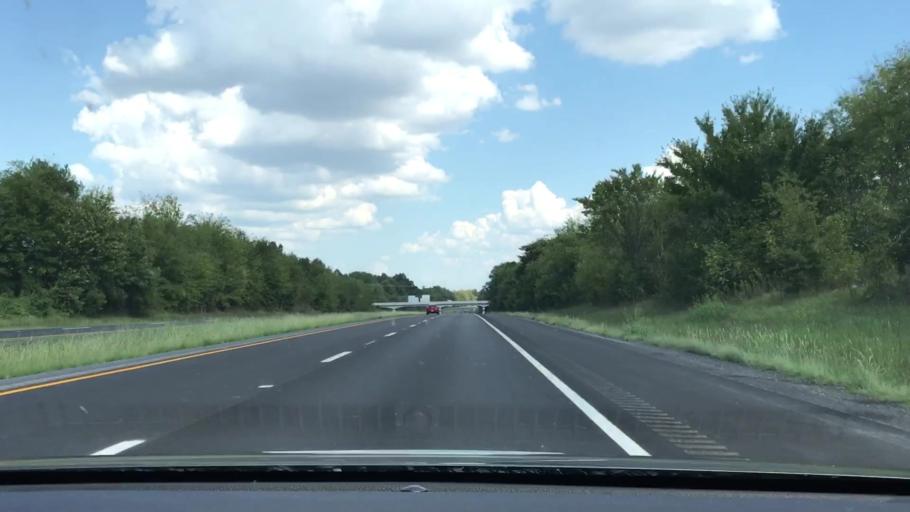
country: US
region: Kentucky
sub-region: Lyon County
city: Eddyville
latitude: 37.0774
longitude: -88.0773
